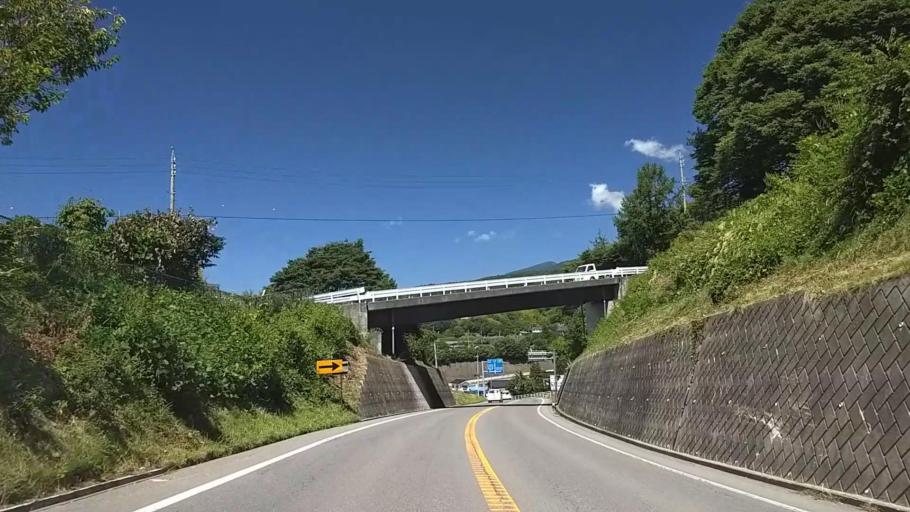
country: JP
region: Nagano
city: Komoro
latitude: 36.3473
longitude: 138.4329
